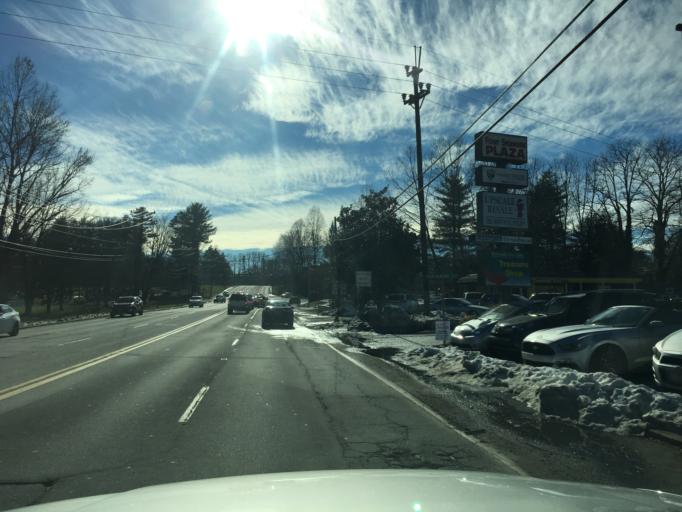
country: US
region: North Carolina
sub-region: Transylvania County
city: Brevard
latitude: 35.2403
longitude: -82.7297
